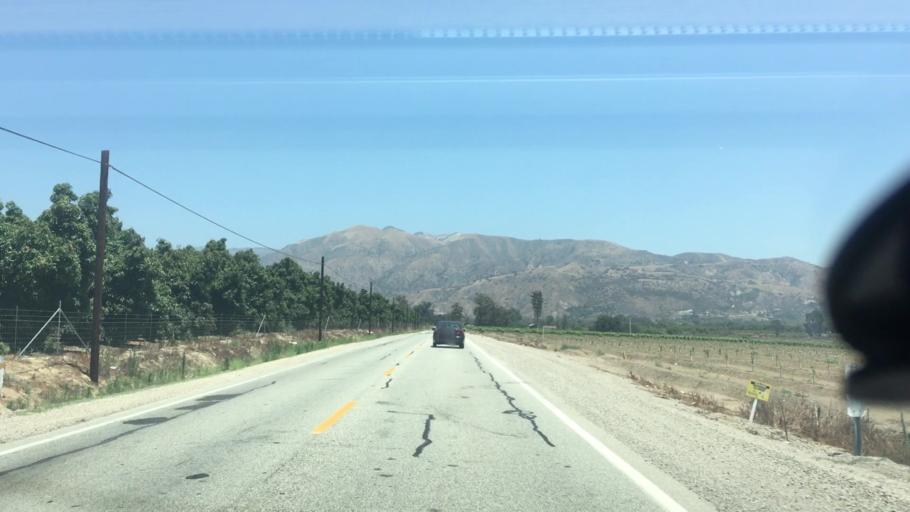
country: US
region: California
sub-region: Ventura County
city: Fillmore
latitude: 34.3954
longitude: -118.9533
